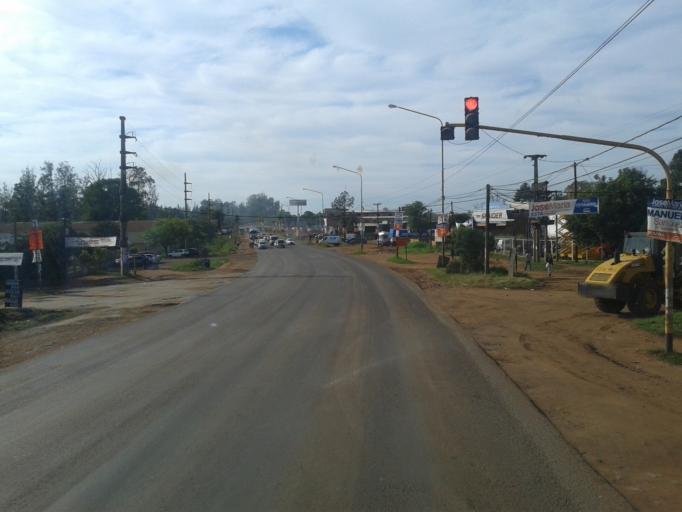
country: AR
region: Misiones
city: Garupa
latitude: -27.4377
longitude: -55.8829
